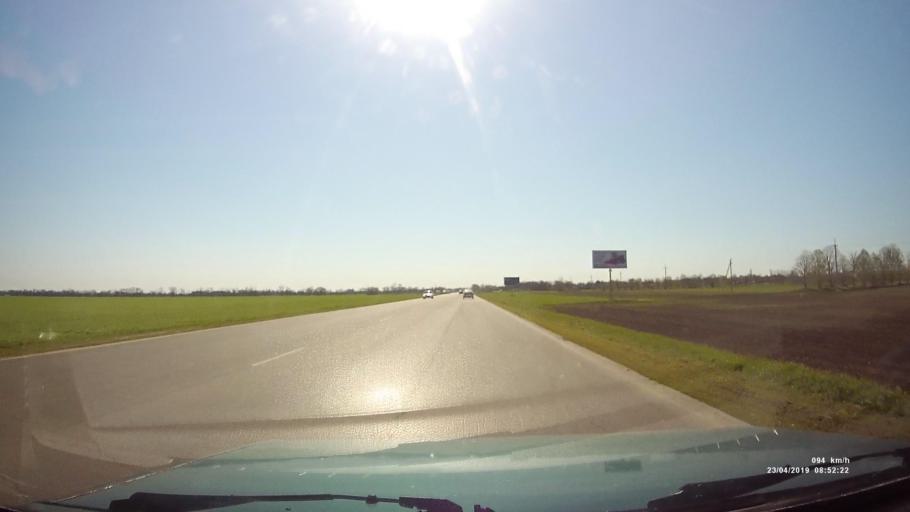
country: RU
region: Rostov
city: Sal'sk
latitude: 46.4820
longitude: 41.4585
